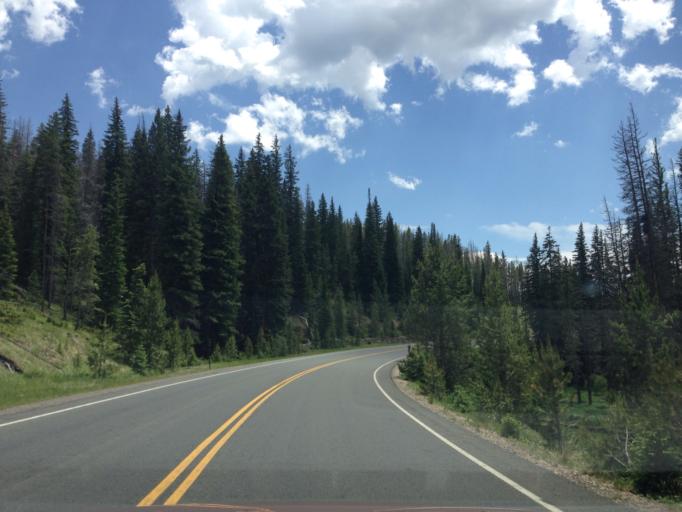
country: US
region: Colorado
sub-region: Grand County
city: Granby
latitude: 40.3423
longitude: -105.8570
